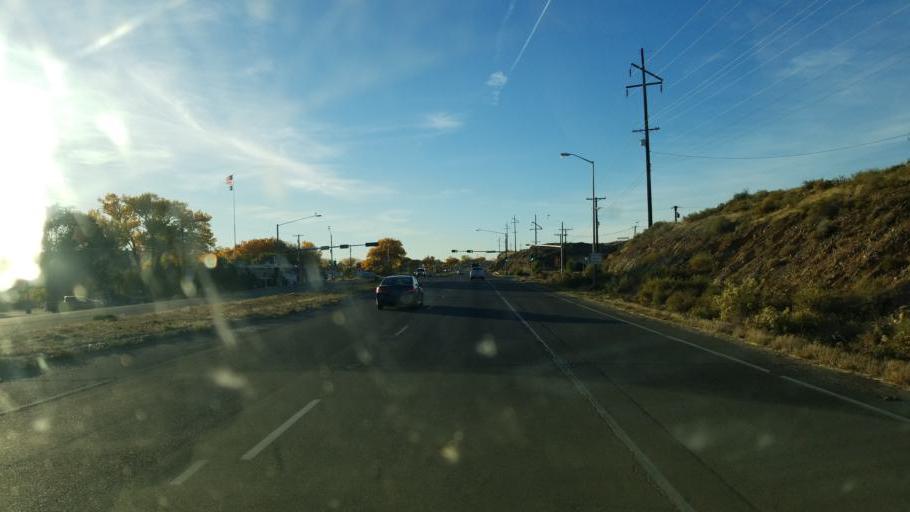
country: US
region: New Mexico
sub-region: San Juan County
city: Farmington
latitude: 36.7097
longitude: -108.1342
